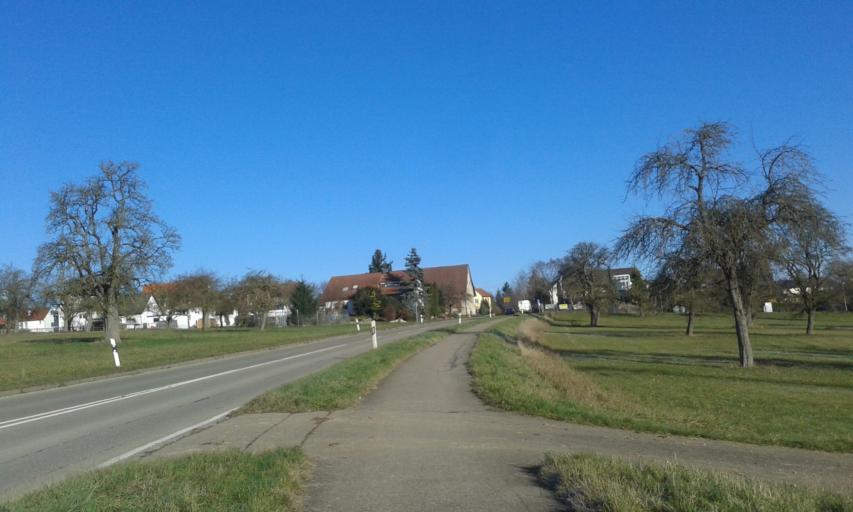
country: DE
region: Baden-Wuerttemberg
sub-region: Tuebingen Region
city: Ulm
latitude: 48.4300
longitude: 9.9695
